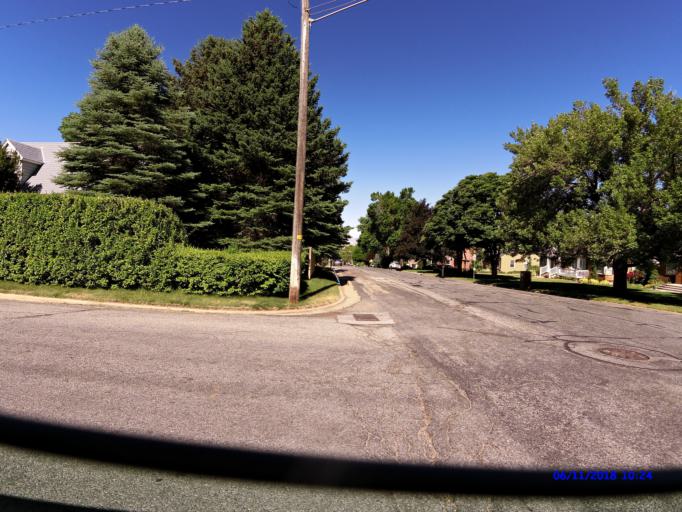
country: US
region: Utah
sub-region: Weber County
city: Ogden
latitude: 41.2119
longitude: -111.9429
